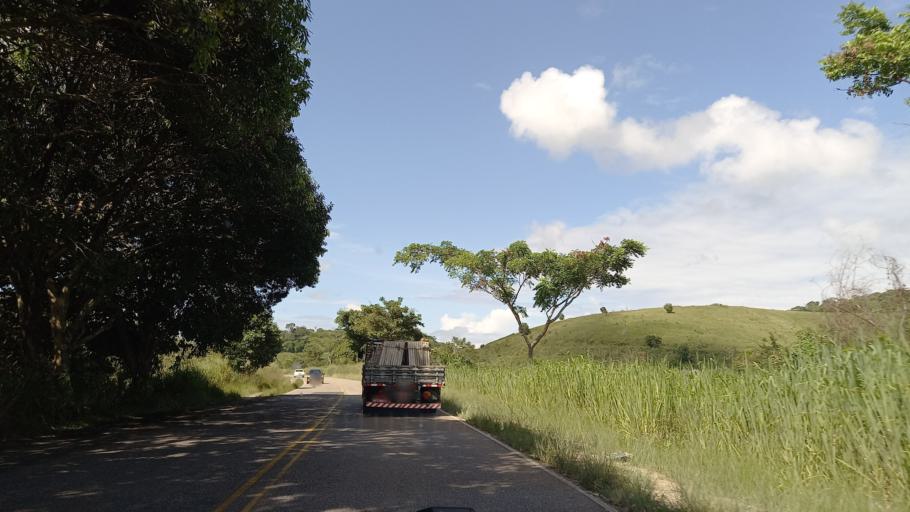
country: BR
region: Pernambuco
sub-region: Barreiros
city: Barreiros
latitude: -8.7839
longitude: -35.1802
